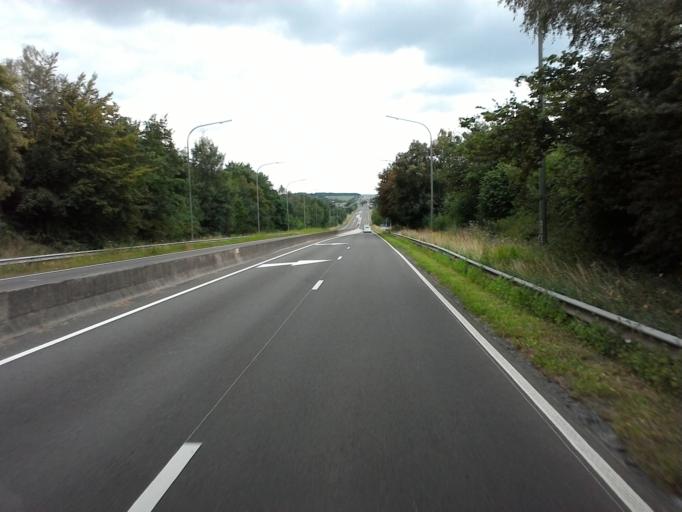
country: BE
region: Wallonia
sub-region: Province du Luxembourg
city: Fauvillers
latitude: 49.9094
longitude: 5.7009
